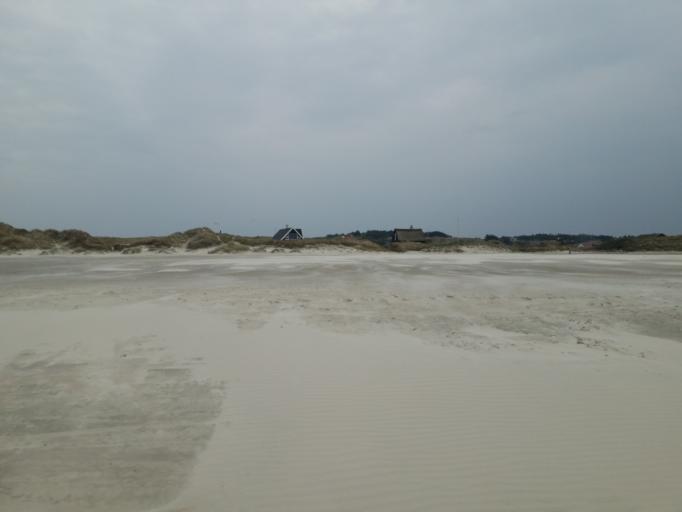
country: DK
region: North Denmark
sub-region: Jammerbugt Kommune
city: Pandrup
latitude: 57.2715
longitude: 9.5977
